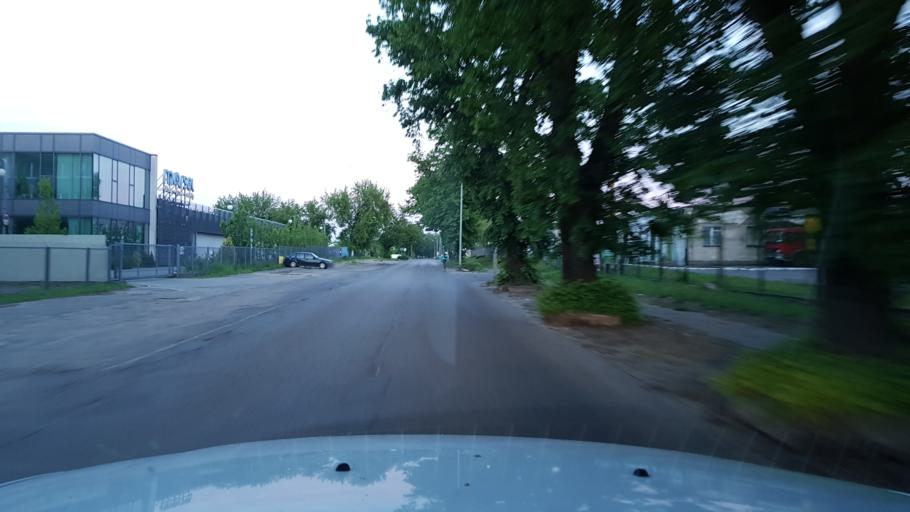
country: PL
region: West Pomeranian Voivodeship
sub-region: Powiat goleniowski
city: Goleniow
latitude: 53.5579
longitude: 14.8458
